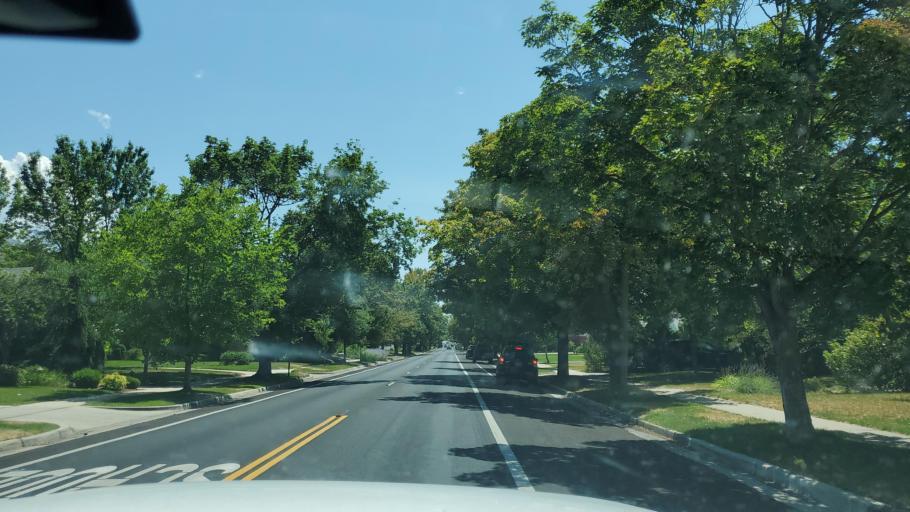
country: US
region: Utah
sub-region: Salt Lake County
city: Willard
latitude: 40.7248
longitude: -111.8309
